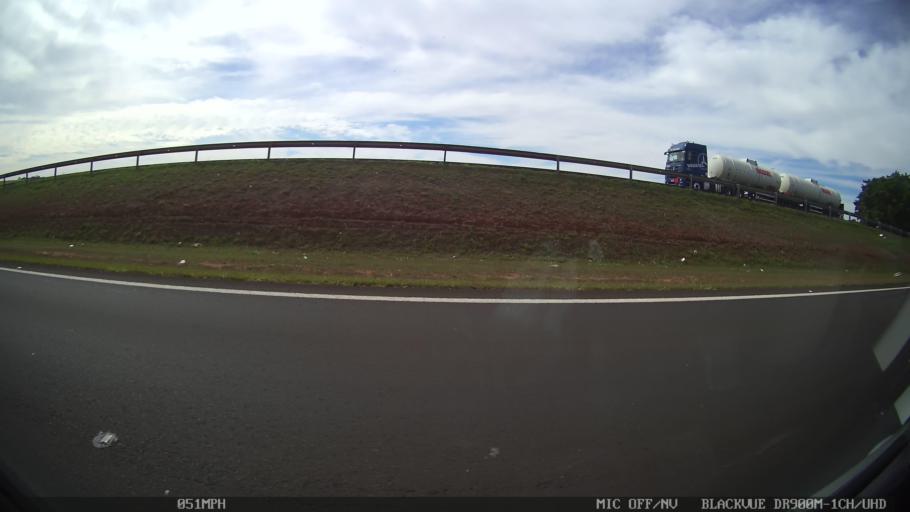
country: BR
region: Sao Paulo
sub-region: Taquaritinga
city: Taquaritinga
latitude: -21.5251
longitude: -48.5269
